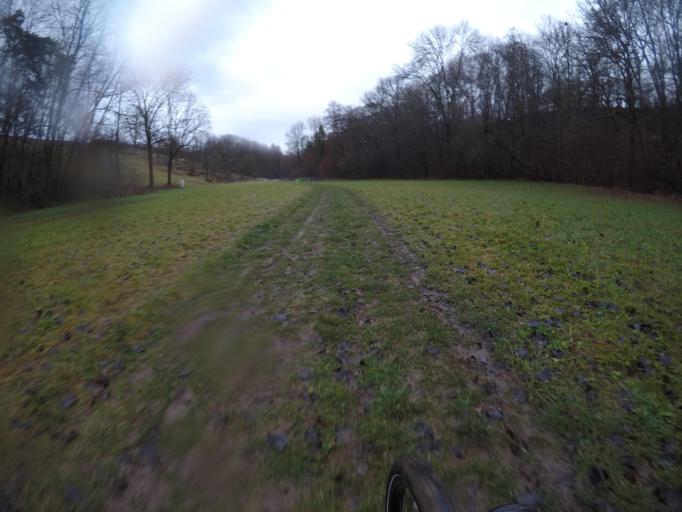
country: DE
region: Baden-Wuerttemberg
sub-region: Regierungsbezirk Stuttgart
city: Bietigheim-Bissingen
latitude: 48.9637
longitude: 9.0838
